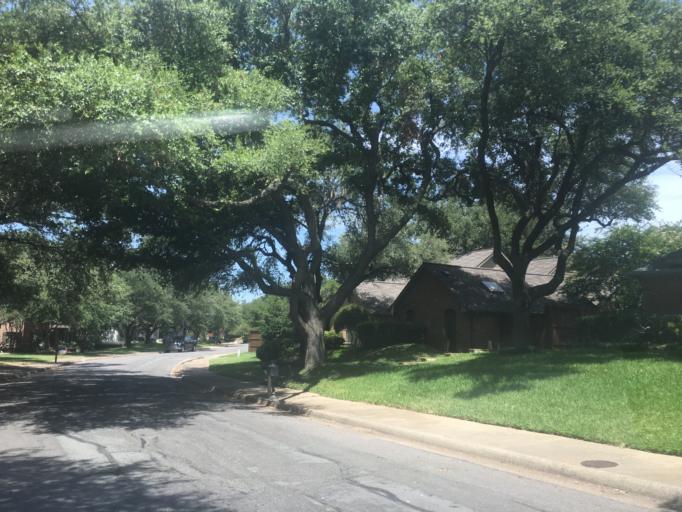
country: US
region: Texas
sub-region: Dallas County
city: Richardson
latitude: 32.8835
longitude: -96.7392
